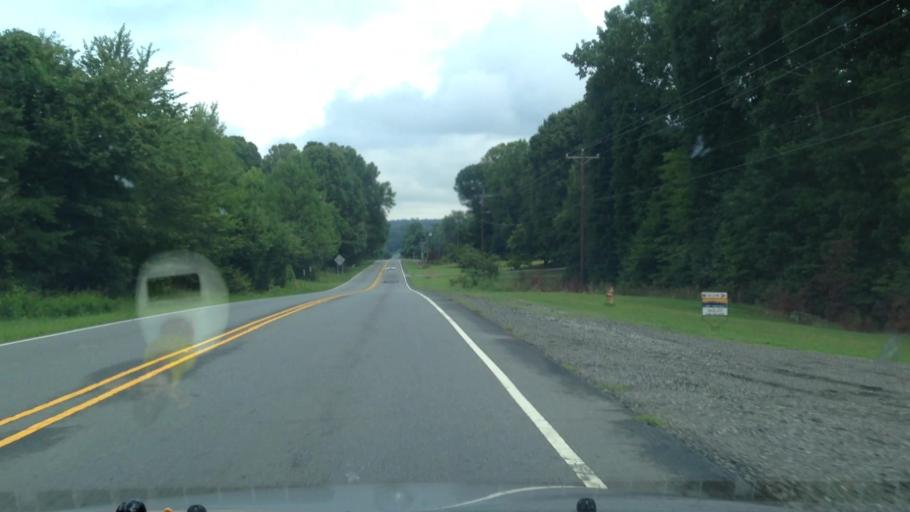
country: US
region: North Carolina
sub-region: Guilford County
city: Stokesdale
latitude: 36.2196
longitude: -80.0544
